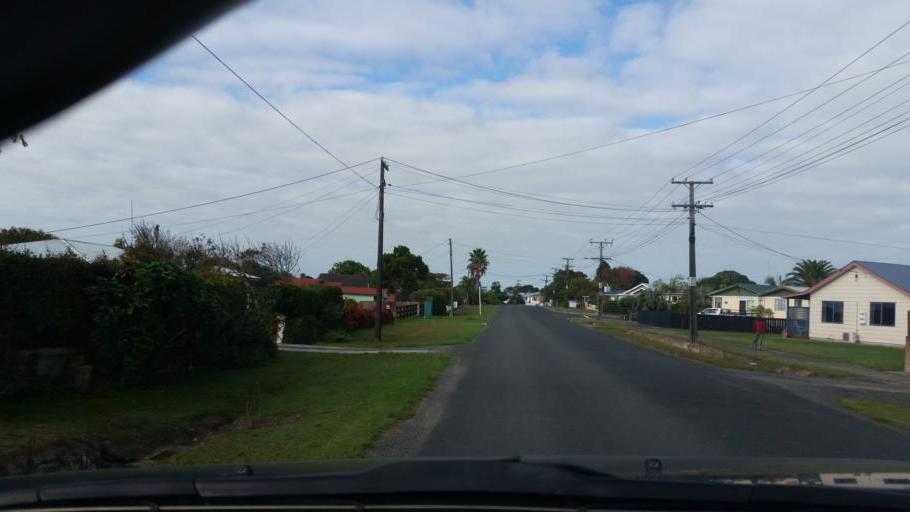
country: NZ
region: Northland
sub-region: Kaipara District
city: Dargaville
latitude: -35.9262
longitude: 173.8688
